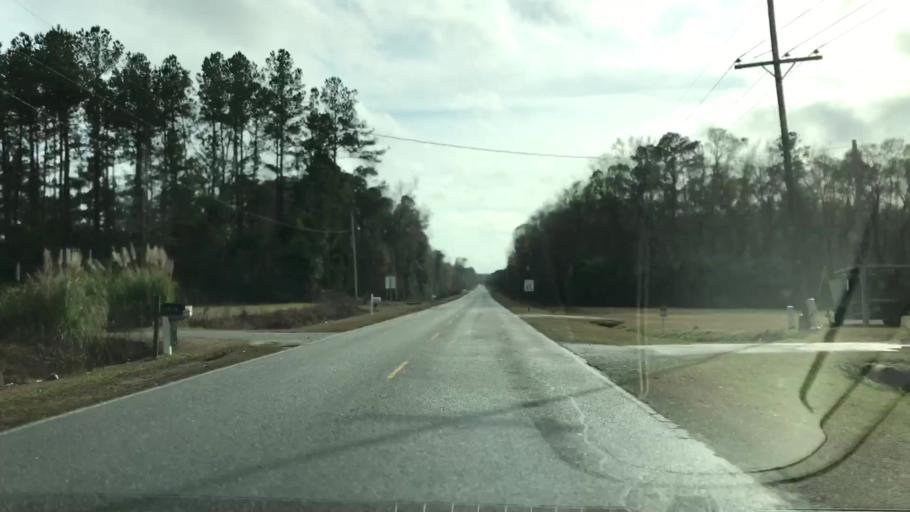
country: US
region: South Carolina
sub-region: Williamsburg County
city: Andrews
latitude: 33.4357
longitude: -79.5926
